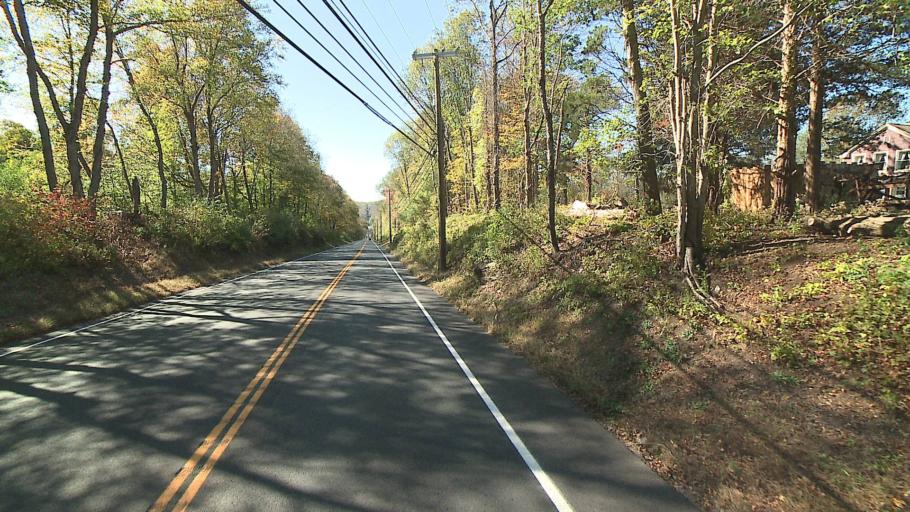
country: US
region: Connecticut
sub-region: Hartford County
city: Terramuggus
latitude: 41.6217
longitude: -72.4662
